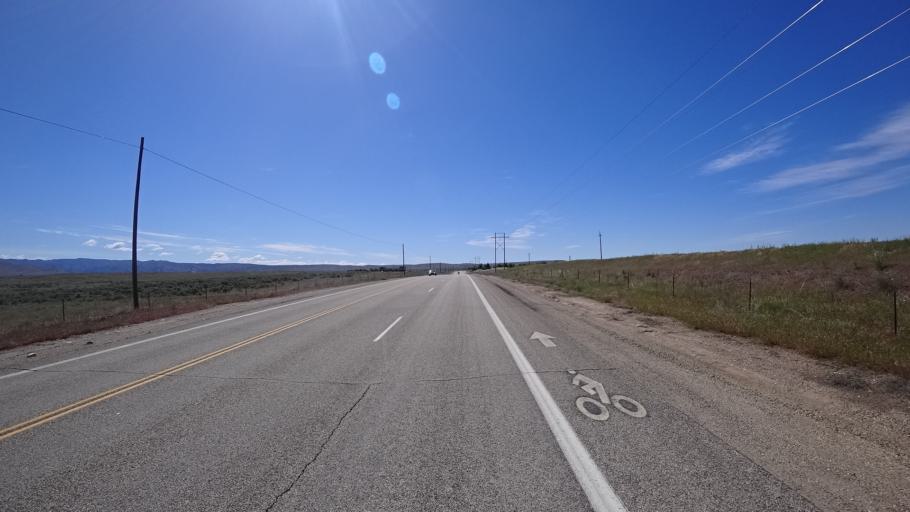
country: US
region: Idaho
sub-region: Ada County
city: Boise
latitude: 43.5375
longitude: -116.1456
